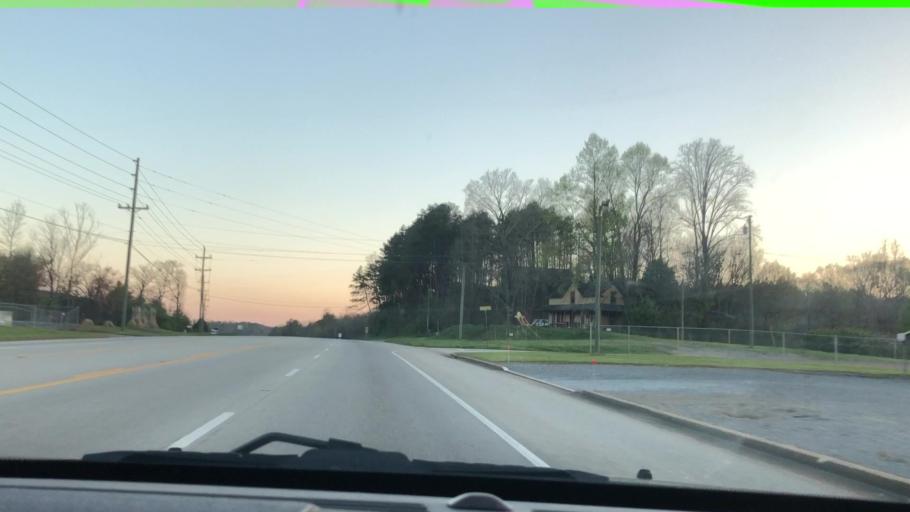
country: US
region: Tennessee
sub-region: Hamilton County
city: Sale Creek
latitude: 35.3664
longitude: -85.1183
